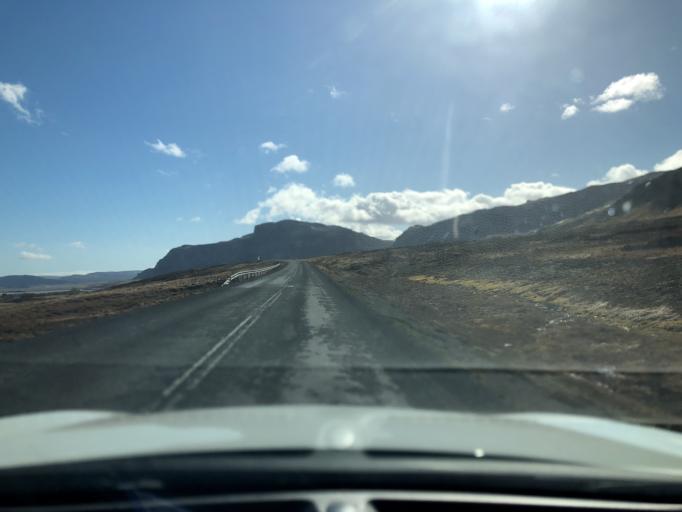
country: IS
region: West
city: Borgarnes
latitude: 64.5247
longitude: -21.8515
